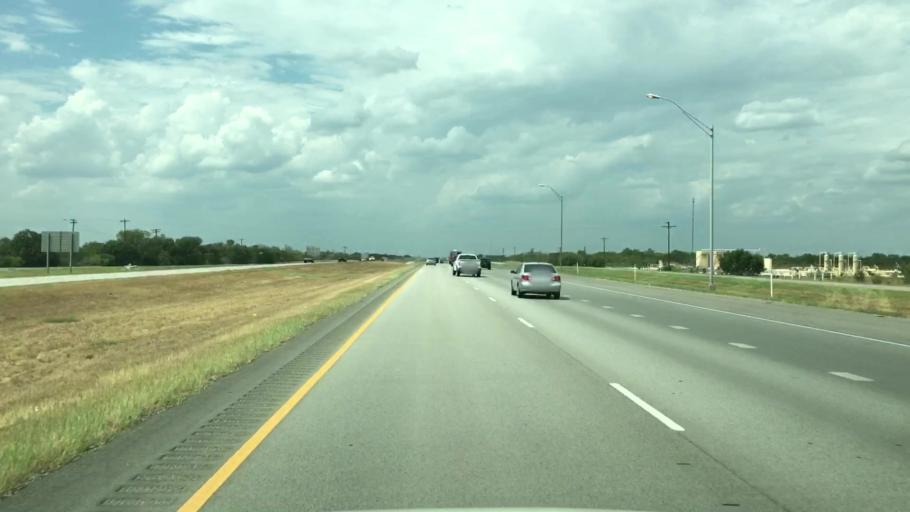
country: US
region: Texas
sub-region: Live Oak County
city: Three Rivers
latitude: 28.5353
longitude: -98.1889
